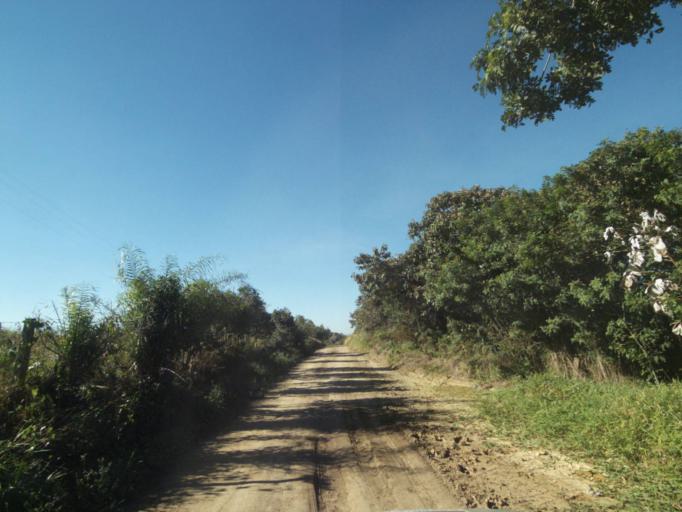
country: BR
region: Parana
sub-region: Tibagi
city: Tibagi
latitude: -24.5765
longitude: -50.4787
